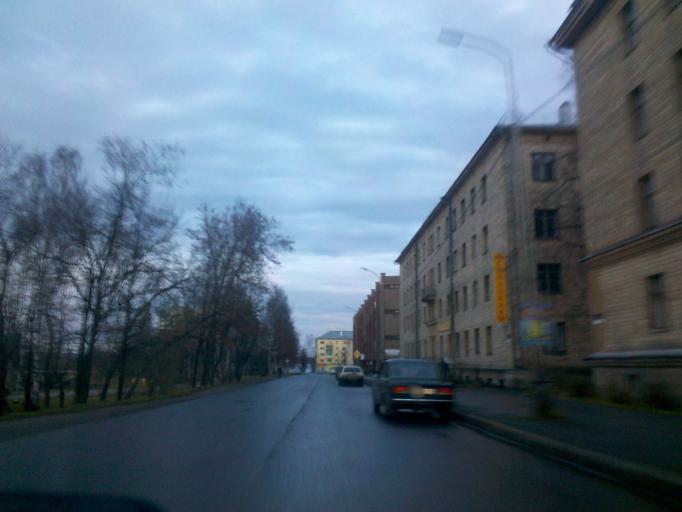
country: RU
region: Republic of Karelia
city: Petrozavodsk
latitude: 61.7838
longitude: 34.3822
